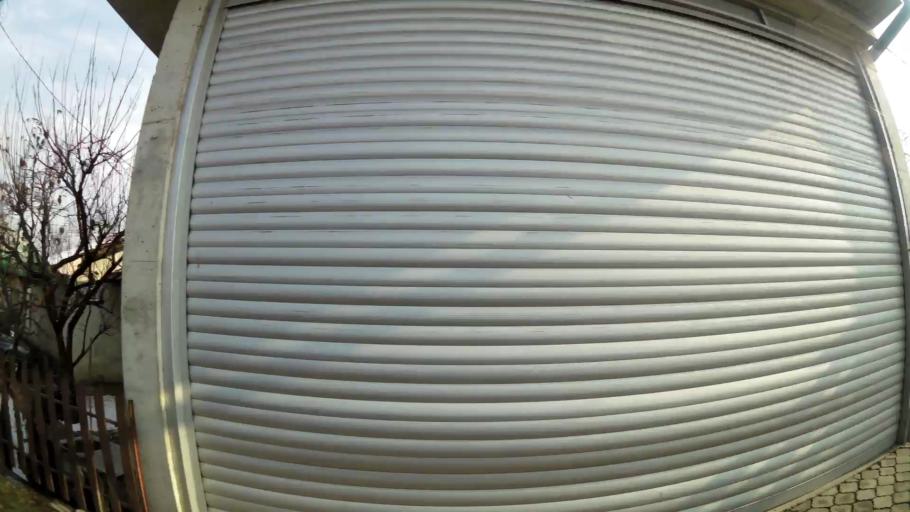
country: MK
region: Kisela Voda
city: Kisela Voda
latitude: 41.9922
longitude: 21.5025
